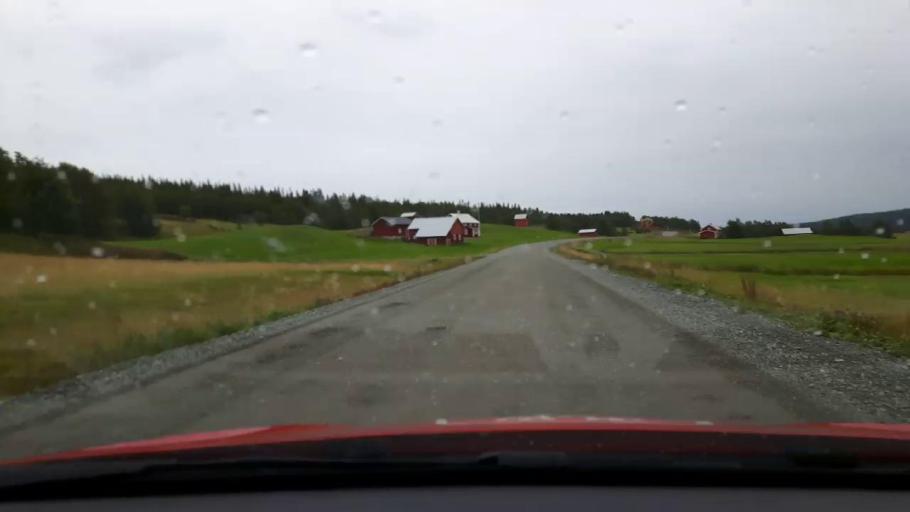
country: NO
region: Nord-Trondelag
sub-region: Meraker
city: Meraker
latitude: 63.5271
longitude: 12.3974
